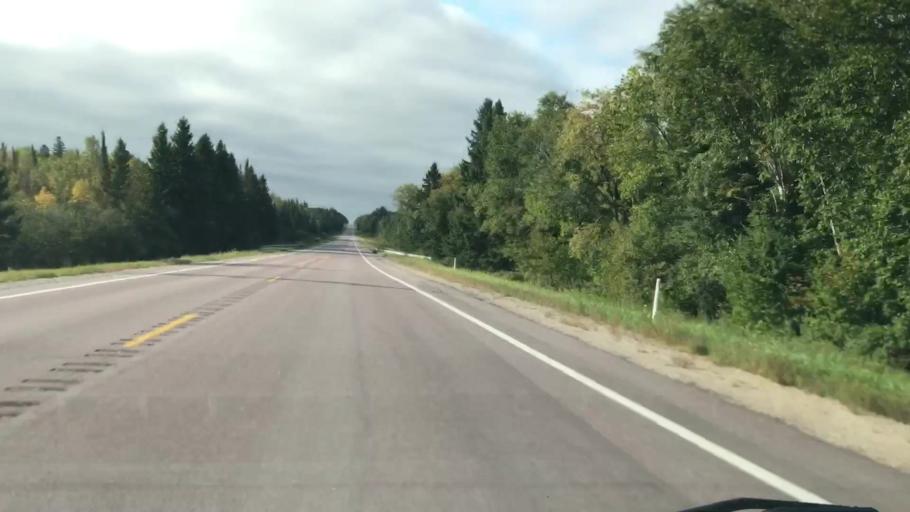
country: US
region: Michigan
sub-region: Luce County
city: Newberry
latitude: 46.3010
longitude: -85.5684
